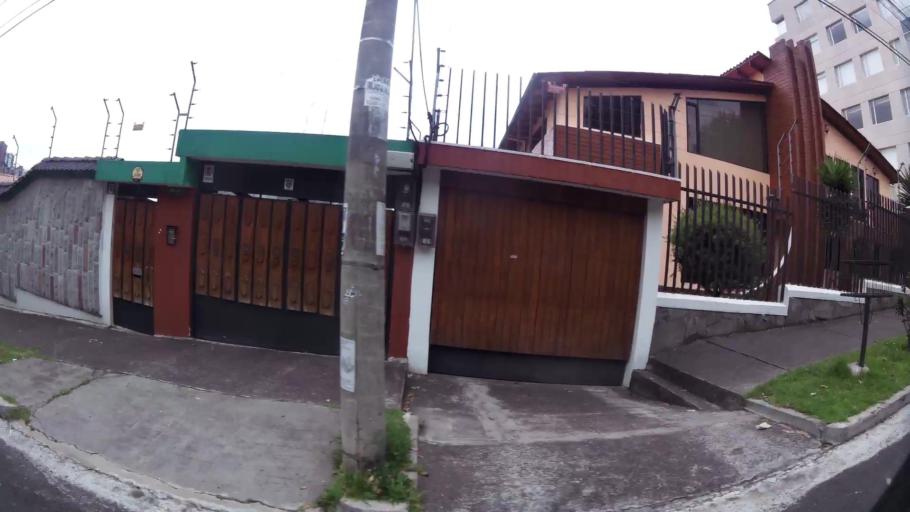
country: EC
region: Pichincha
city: Quito
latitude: -0.1721
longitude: -78.4989
